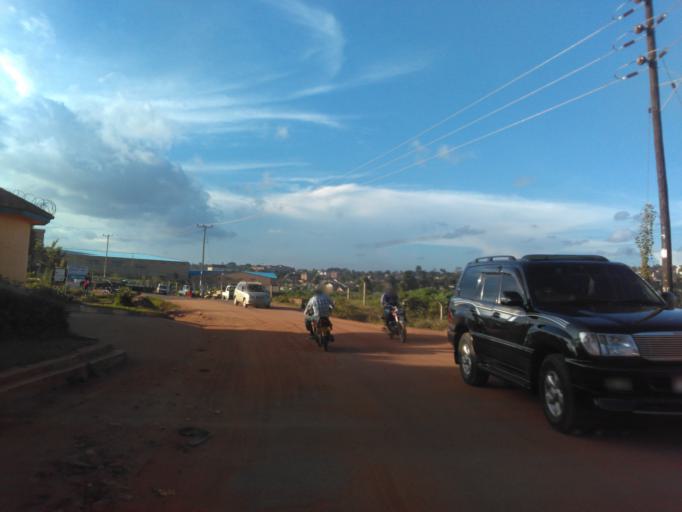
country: UG
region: Central Region
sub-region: Kampala District
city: Kampala
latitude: 0.2678
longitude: 32.5575
